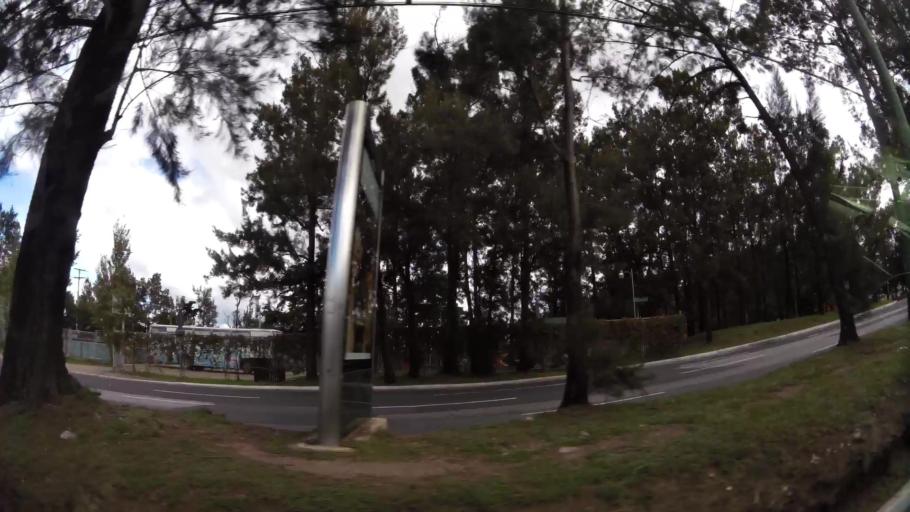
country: GT
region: Guatemala
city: Santa Catarina Pinula
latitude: 14.5959
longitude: -90.4961
